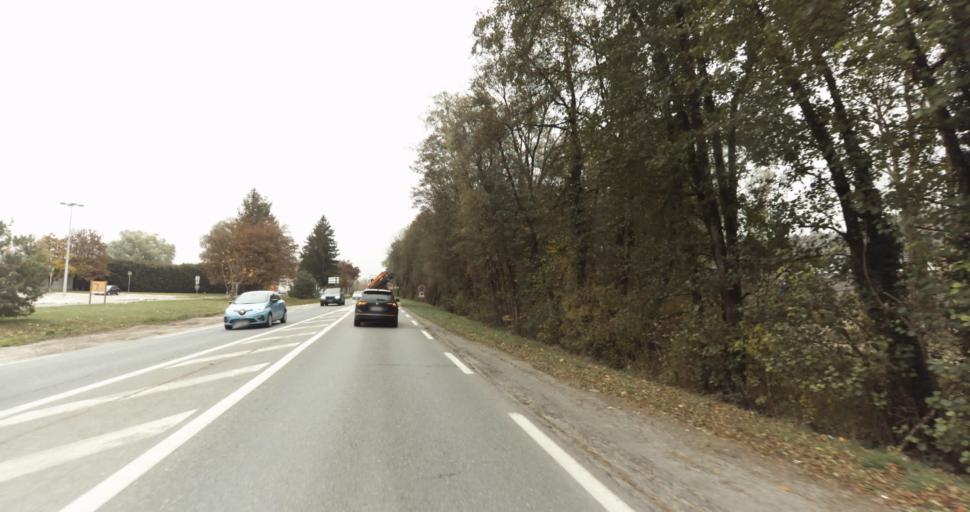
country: FR
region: Rhone-Alpes
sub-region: Departement de la Haute-Savoie
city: Poisy
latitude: 45.9365
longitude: 6.0736
